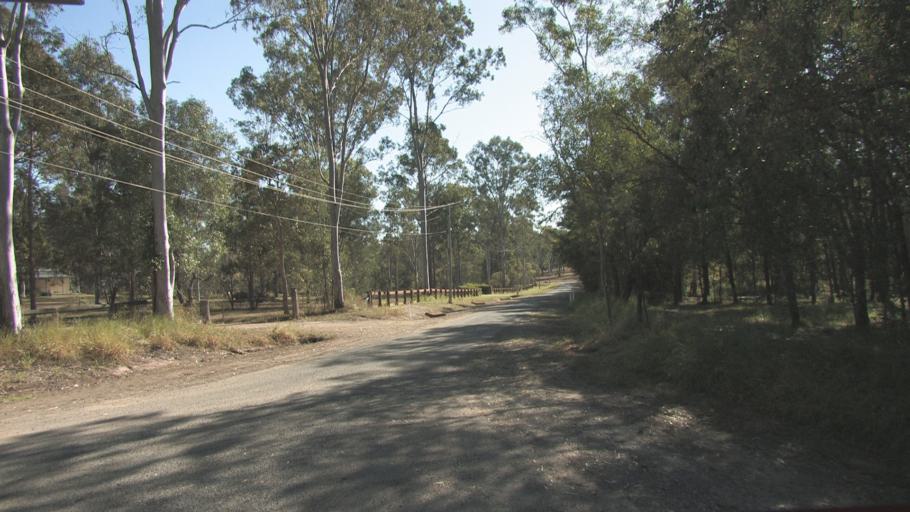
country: AU
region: Queensland
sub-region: Logan
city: Cedar Vale
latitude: -27.8446
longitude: 153.0400
